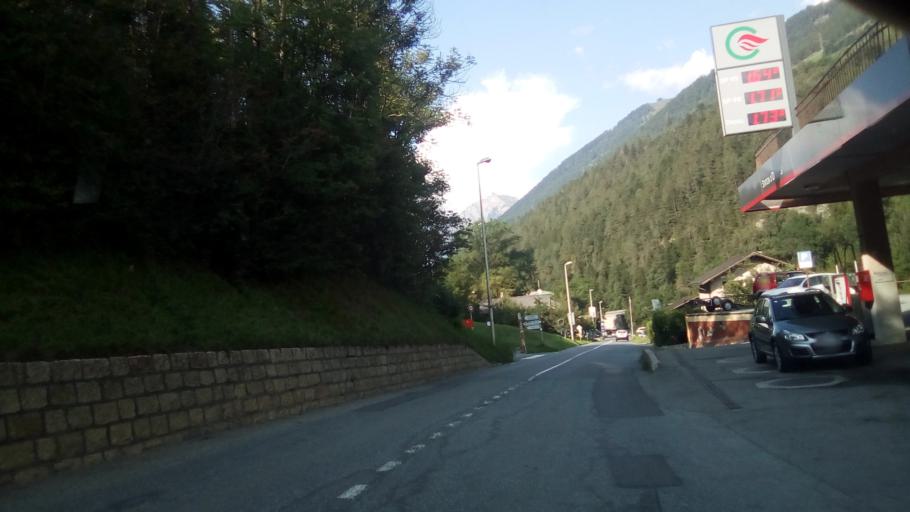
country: CH
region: Valais
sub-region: Entremont District
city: Orsieres
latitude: 46.0346
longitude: 7.1449
